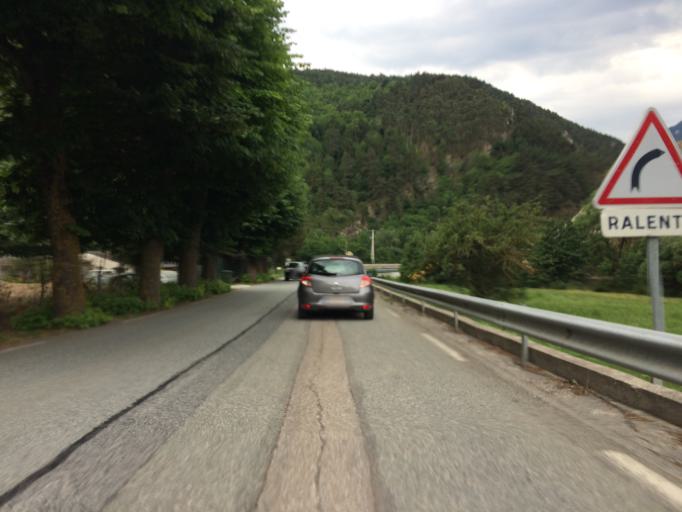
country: FR
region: Provence-Alpes-Cote d'Azur
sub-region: Departement des Alpes-Maritimes
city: Tende
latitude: 44.0747
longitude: 7.5988
